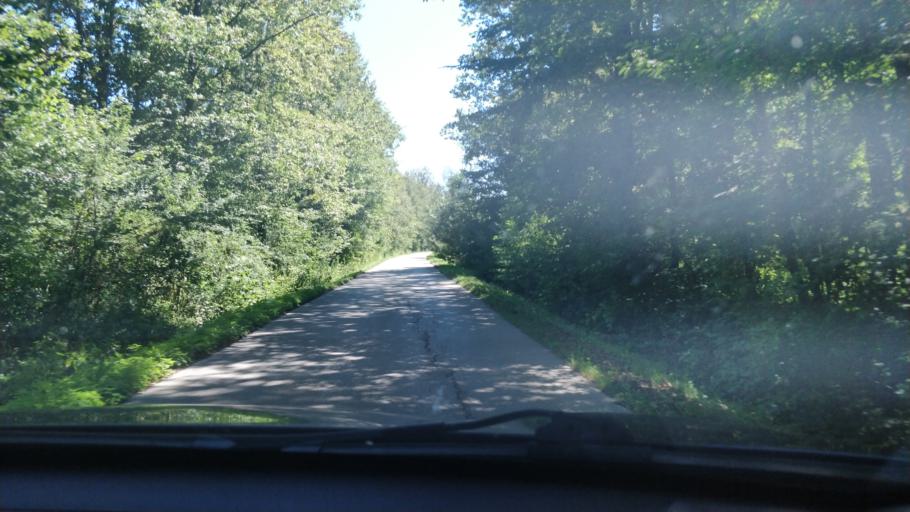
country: HR
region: Karlovacka
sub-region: Grad Karlovac
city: Karlovac
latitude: 45.4711
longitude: 15.6625
